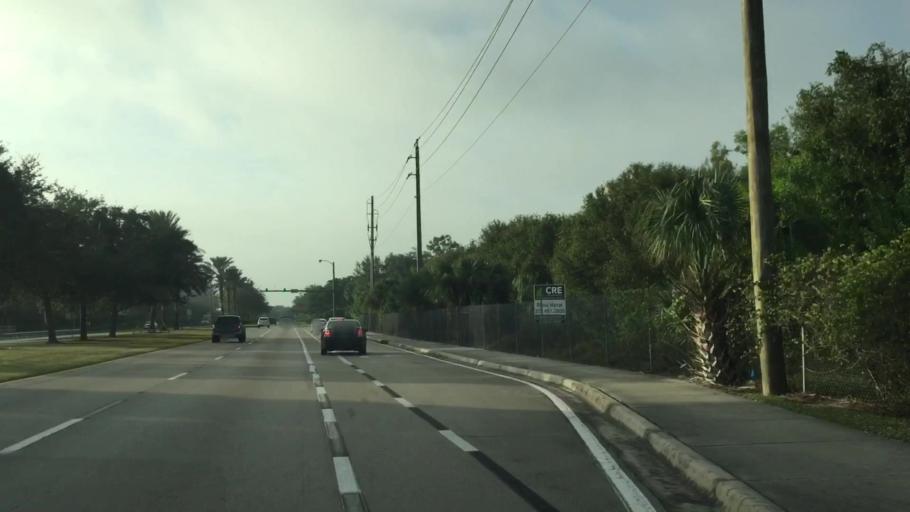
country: US
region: Florida
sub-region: Lee County
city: Estero
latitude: 26.4217
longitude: -81.7885
